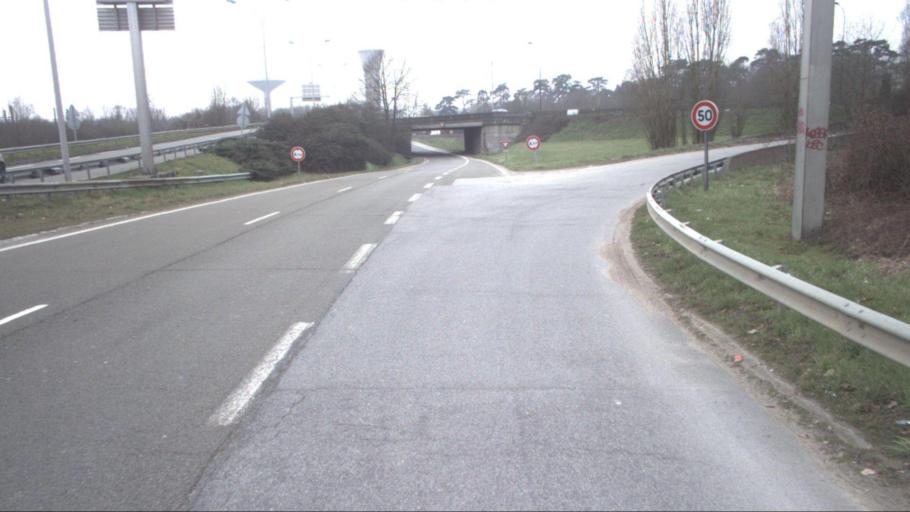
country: FR
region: Ile-de-France
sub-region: Departement des Yvelines
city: Montigny-le-Bretonneux
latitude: 48.7847
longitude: 2.0360
